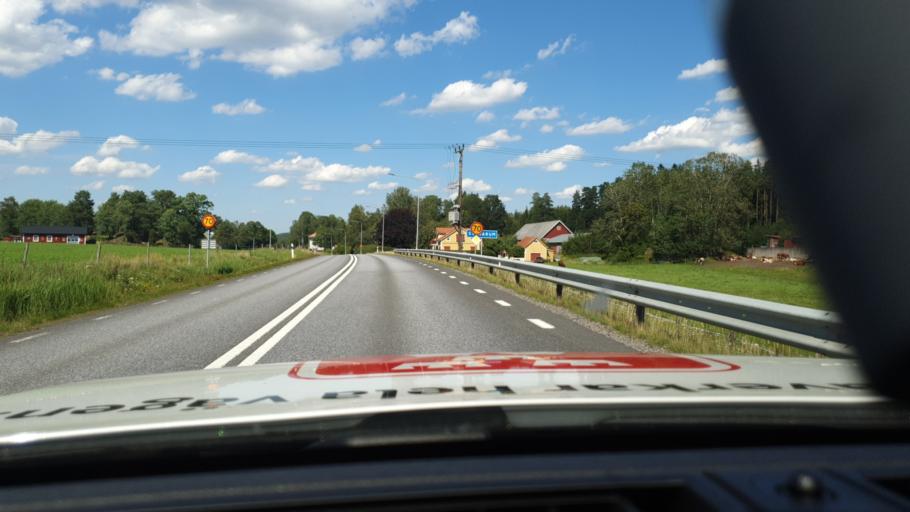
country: SE
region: Joenkoeping
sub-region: Vaggeryds Kommun
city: Vaggeryd
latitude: 57.4663
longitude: 14.3171
